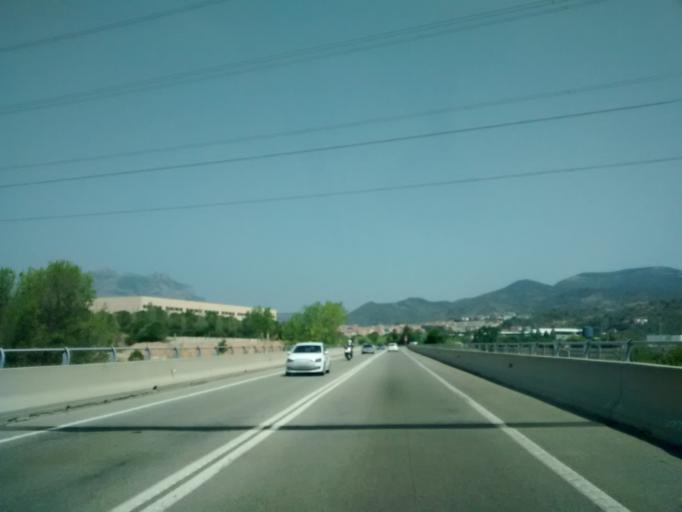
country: ES
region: Catalonia
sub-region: Provincia de Barcelona
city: Abrera
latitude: 41.5285
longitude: 1.9056
